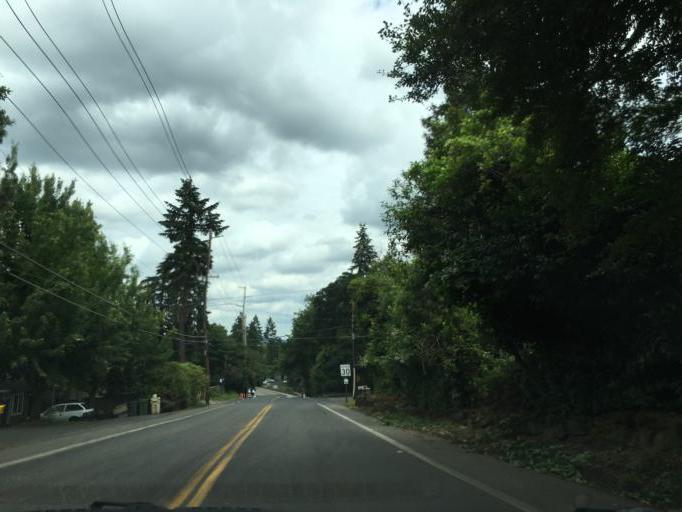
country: US
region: Oregon
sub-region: Clackamas County
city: Lake Oswego
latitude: 45.4094
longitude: -122.6700
